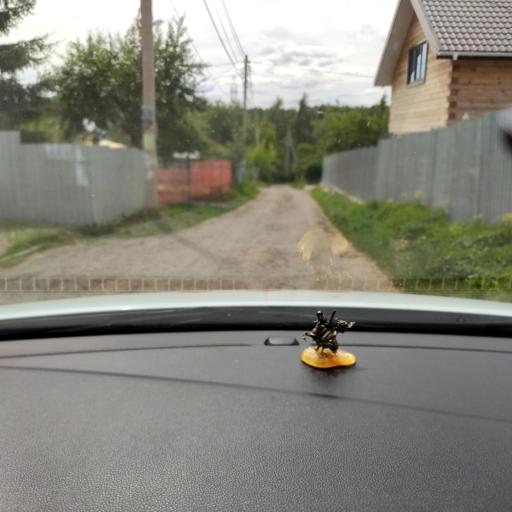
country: RU
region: Tatarstan
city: Staroye Arakchino
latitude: 55.8908
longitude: 49.0428
